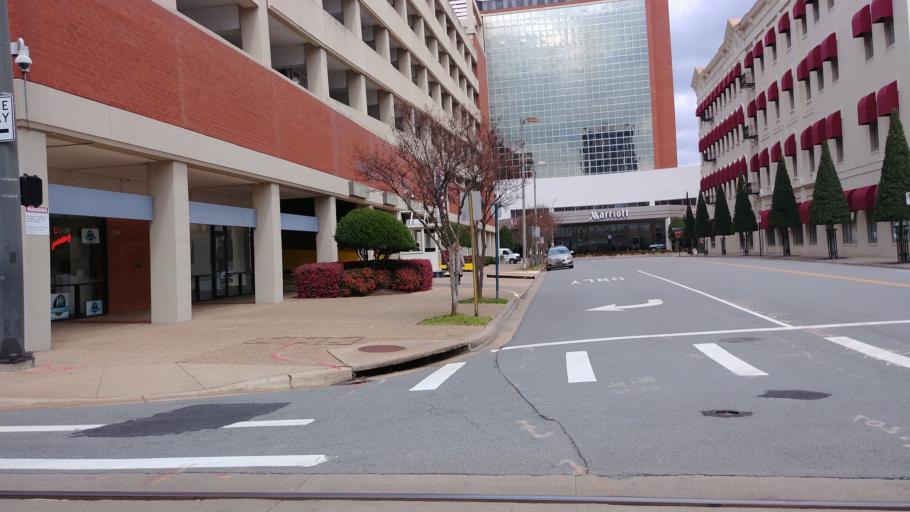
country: US
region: Arkansas
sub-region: Pulaski County
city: Little Rock
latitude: 34.7472
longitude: -92.2718
